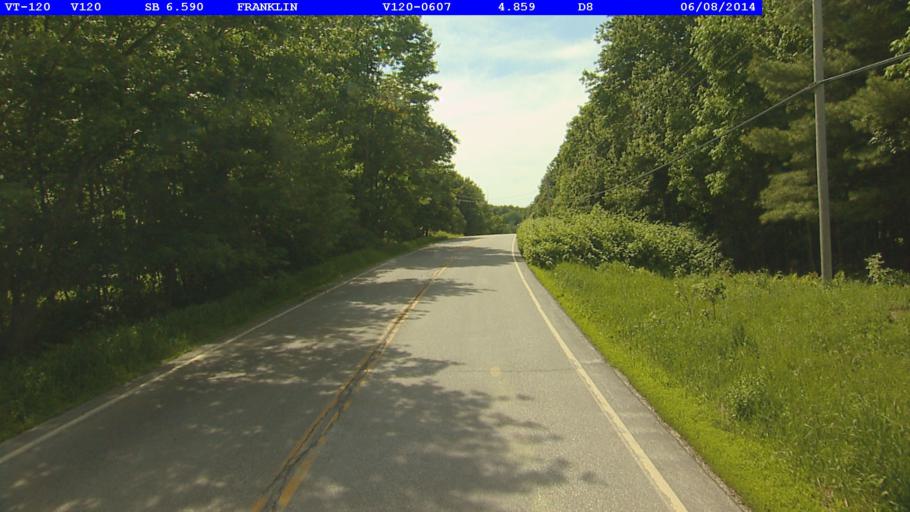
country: US
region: Vermont
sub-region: Franklin County
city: Enosburg Falls
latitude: 44.9863
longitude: -72.8963
